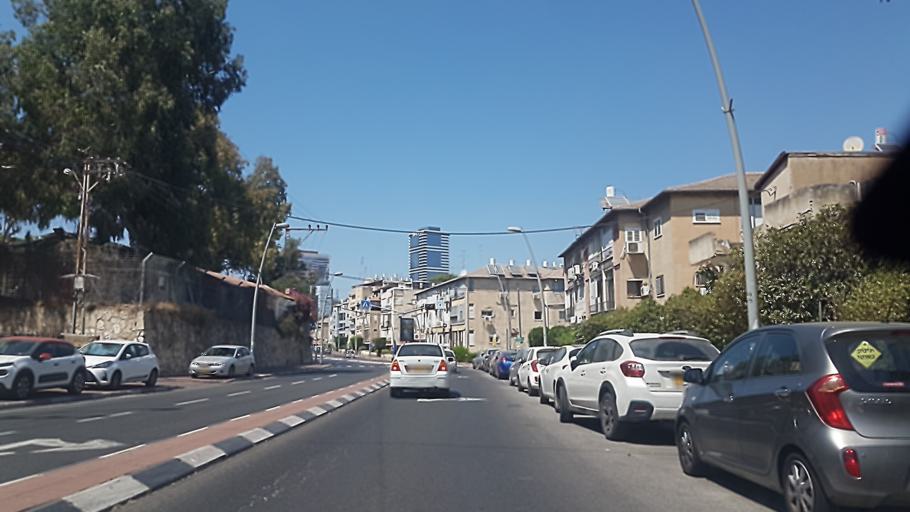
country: IL
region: Tel Aviv
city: Ramat Gan
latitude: 32.0842
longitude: 34.8219
